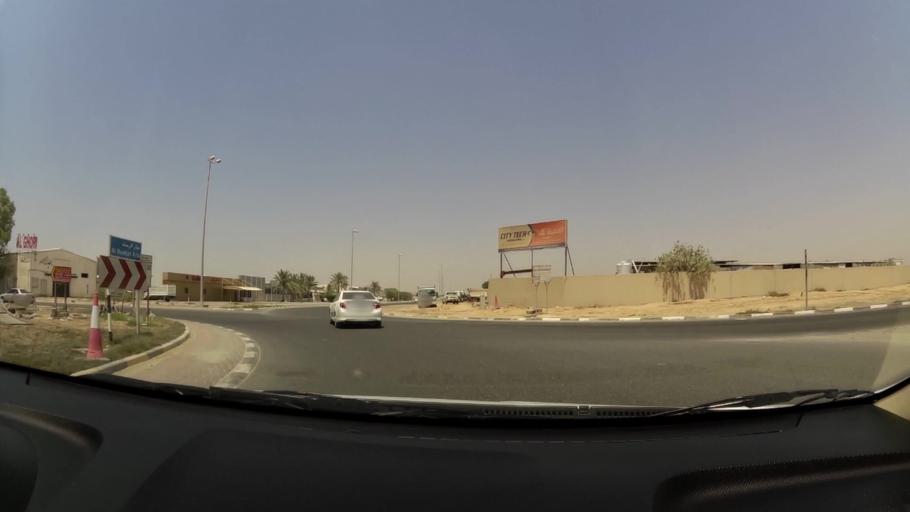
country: AE
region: Umm al Qaywayn
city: Umm al Qaywayn
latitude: 25.4992
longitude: 55.5629
